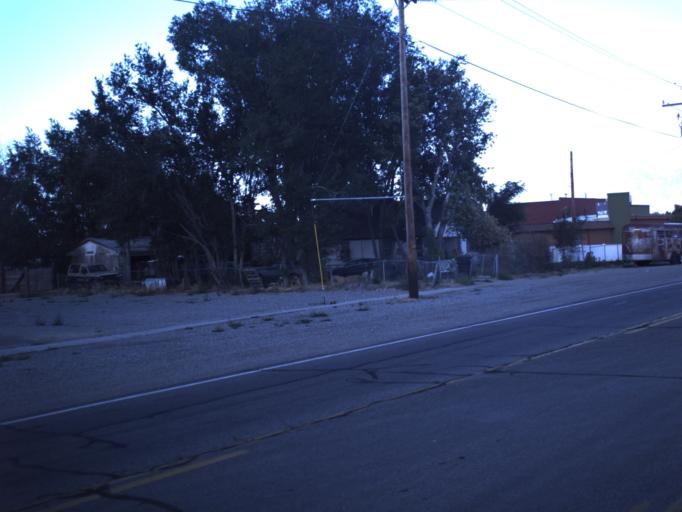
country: US
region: Utah
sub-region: Tooele County
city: Grantsville
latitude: 40.5997
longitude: -112.4419
